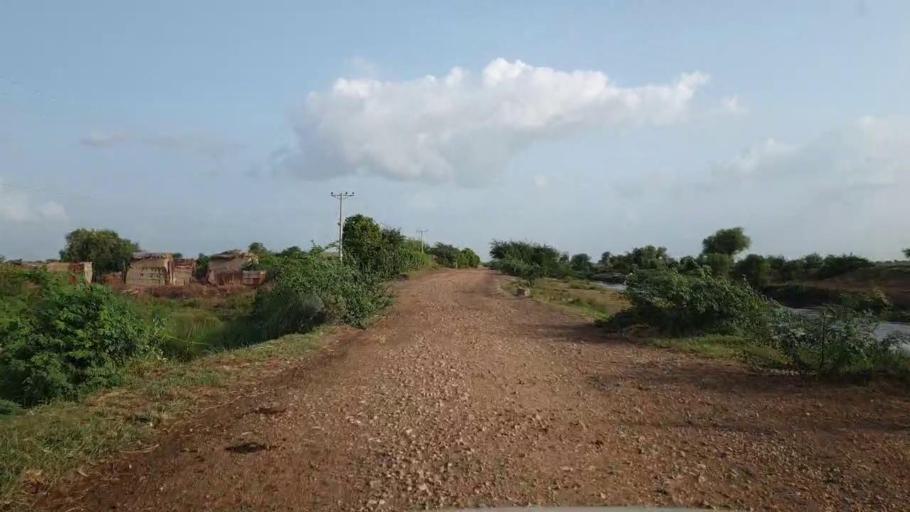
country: PK
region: Sindh
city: Kario
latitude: 24.8186
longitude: 68.6466
